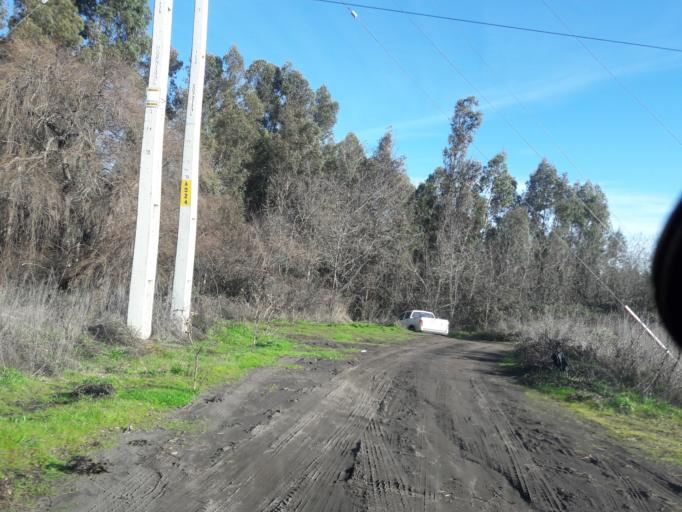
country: CL
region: Biobio
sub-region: Provincia de Biobio
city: Cabrero
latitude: -37.0249
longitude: -72.1909
